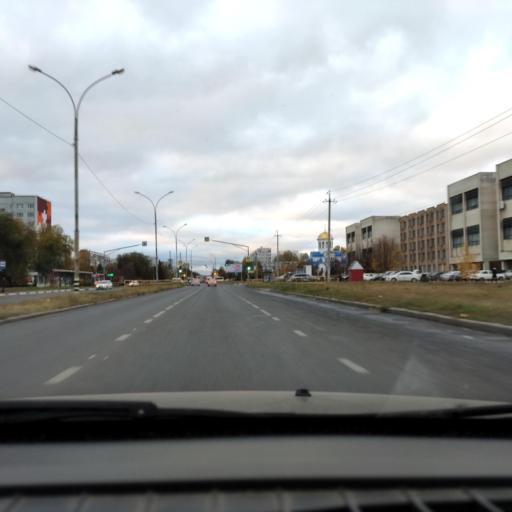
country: RU
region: Samara
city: Tol'yatti
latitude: 53.5373
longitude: 49.3145
